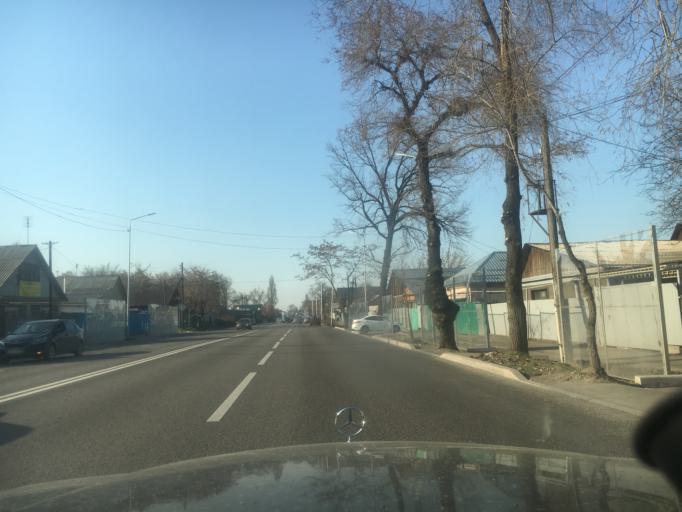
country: KZ
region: Almaty Qalasy
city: Almaty
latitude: 43.2807
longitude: 76.9399
